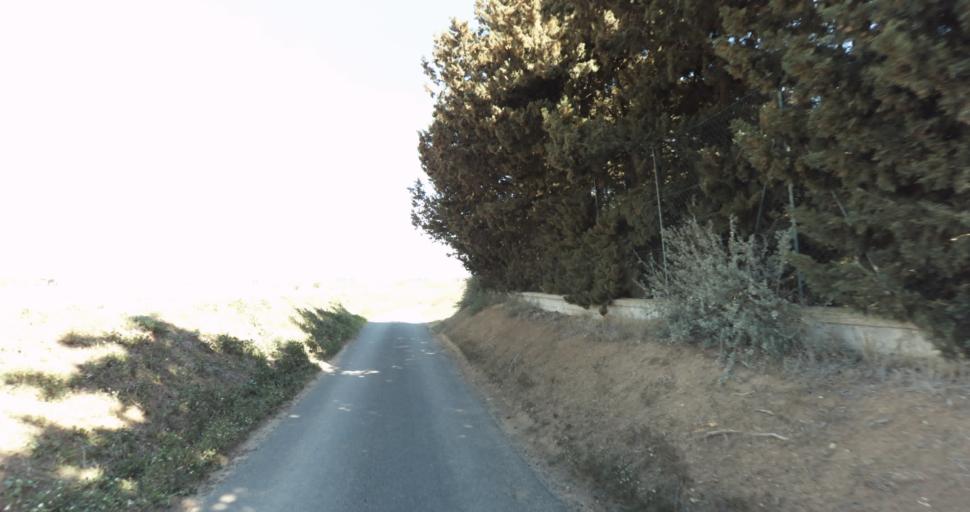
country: FR
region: Languedoc-Roussillon
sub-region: Departement de l'Herault
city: Marseillan
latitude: 43.3706
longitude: 3.5391
